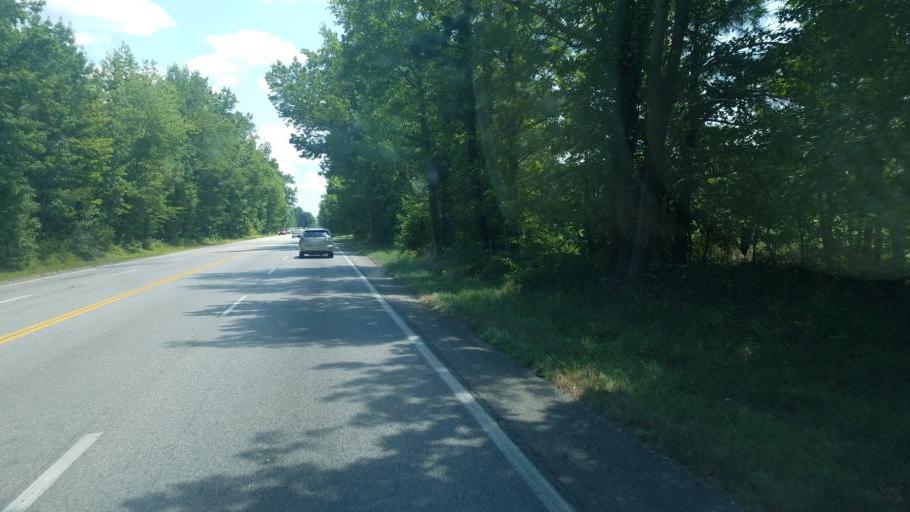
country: US
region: Virginia
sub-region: Prince George County
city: Prince George
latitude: 37.1126
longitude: -77.2084
